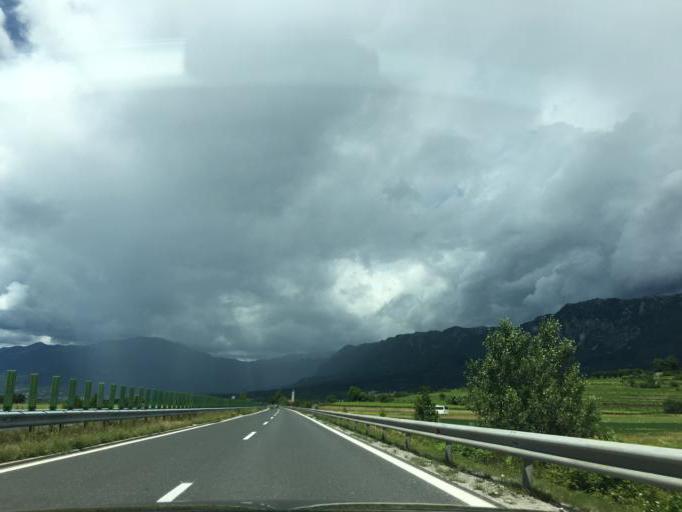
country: SI
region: Vipava
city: Vipava
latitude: 45.8500
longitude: 13.9476
